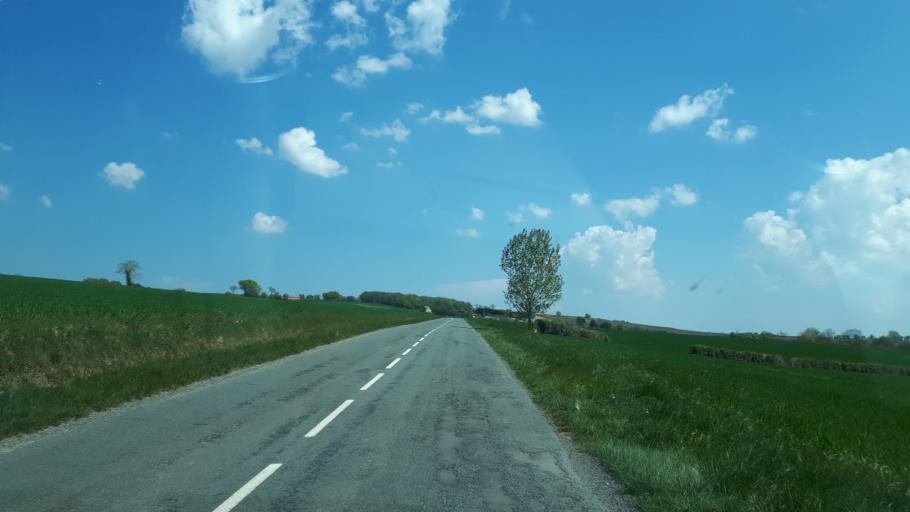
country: FR
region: Centre
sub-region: Departement du Cher
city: Sancerre
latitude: 47.3045
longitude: 2.7169
